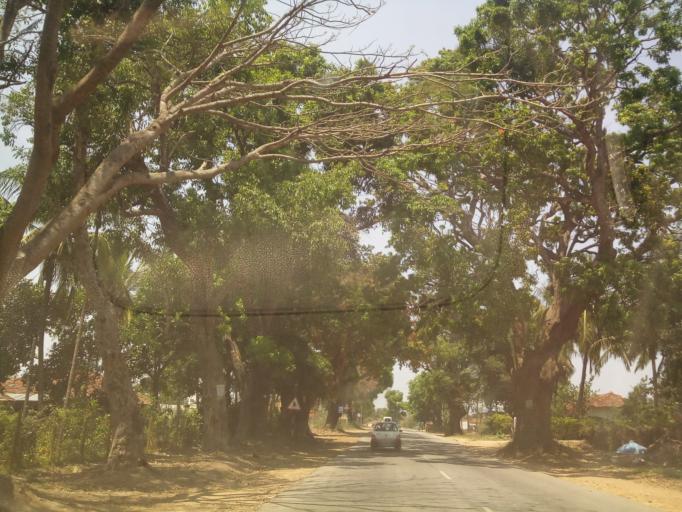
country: IN
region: Karnataka
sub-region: Hassan
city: Alur
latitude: 12.9492
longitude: 75.9436
